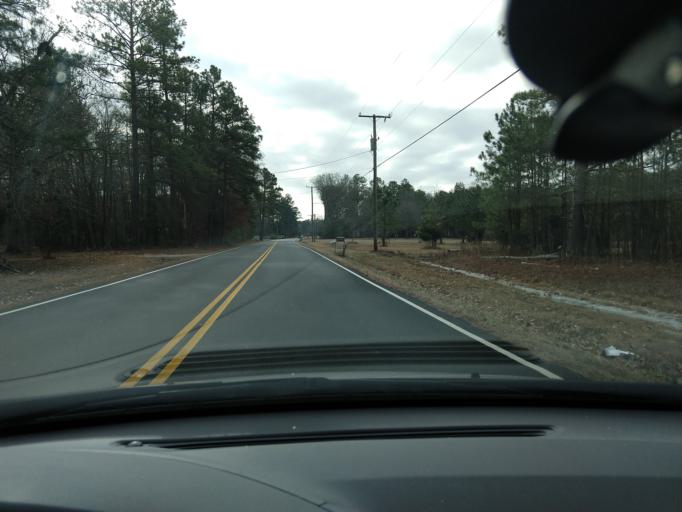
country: US
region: Virginia
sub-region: Henrico County
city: Fort Lee
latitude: 37.4469
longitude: -77.3693
